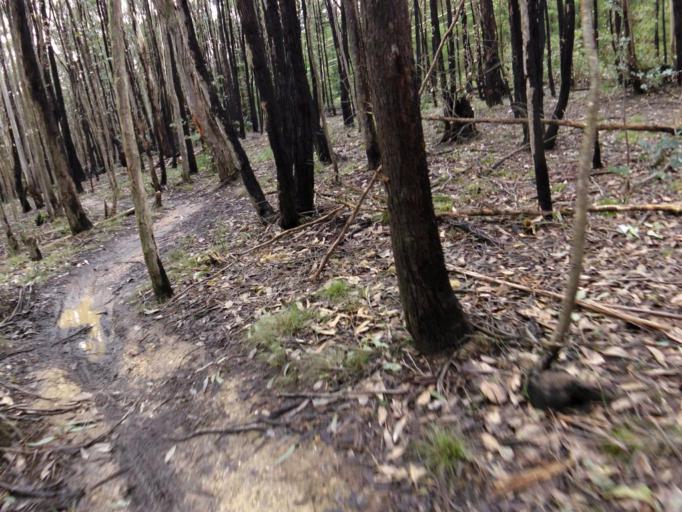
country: AU
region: Victoria
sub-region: Moorabool
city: Bacchus Marsh
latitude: -37.4149
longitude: 144.4964
